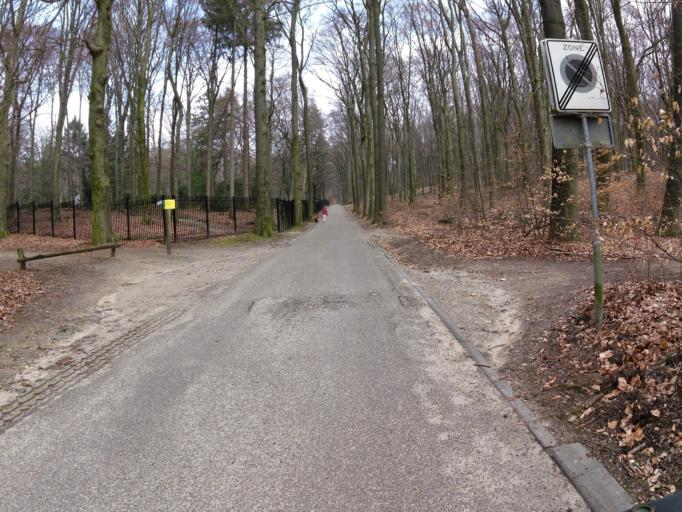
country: NL
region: Gelderland
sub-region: Gemeente Rozendaal
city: Rozendaal
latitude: 52.0115
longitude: 5.9700
